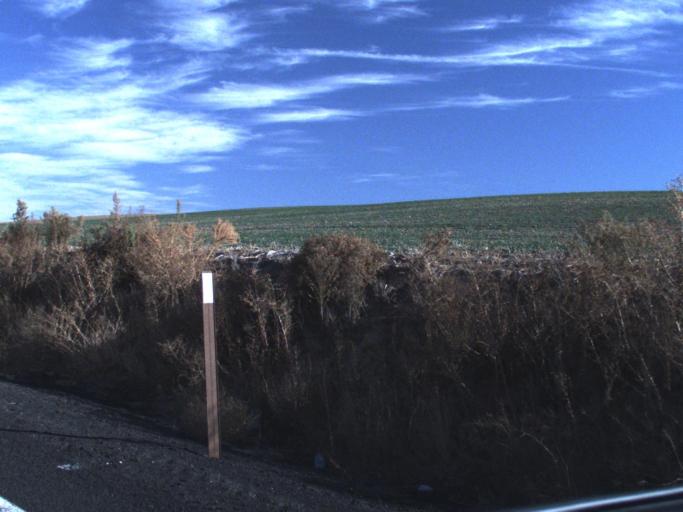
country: US
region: Washington
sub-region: Adams County
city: Ritzville
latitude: 47.1847
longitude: -118.6870
